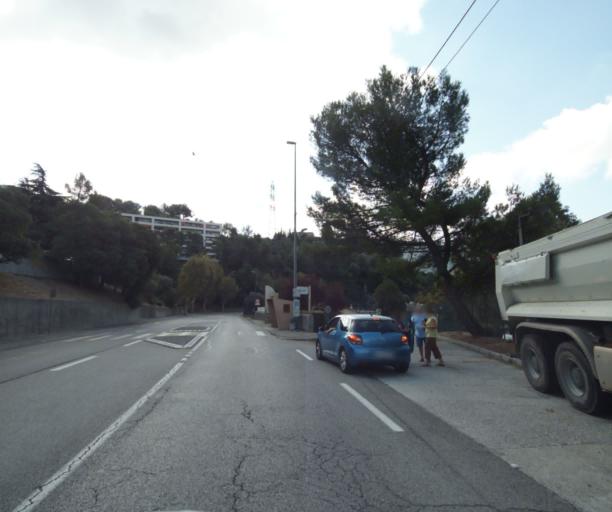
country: FR
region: Provence-Alpes-Cote d'Azur
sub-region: Departement des Alpes-Maritimes
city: Drap
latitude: 43.7490
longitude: 7.3204
